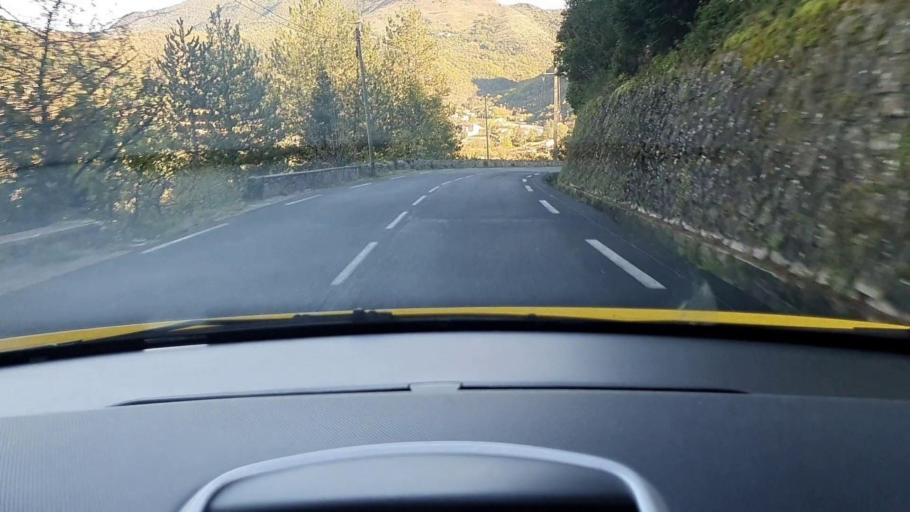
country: FR
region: Languedoc-Roussillon
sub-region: Departement du Gard
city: Sumene
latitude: 43.9847
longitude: 3.7102
